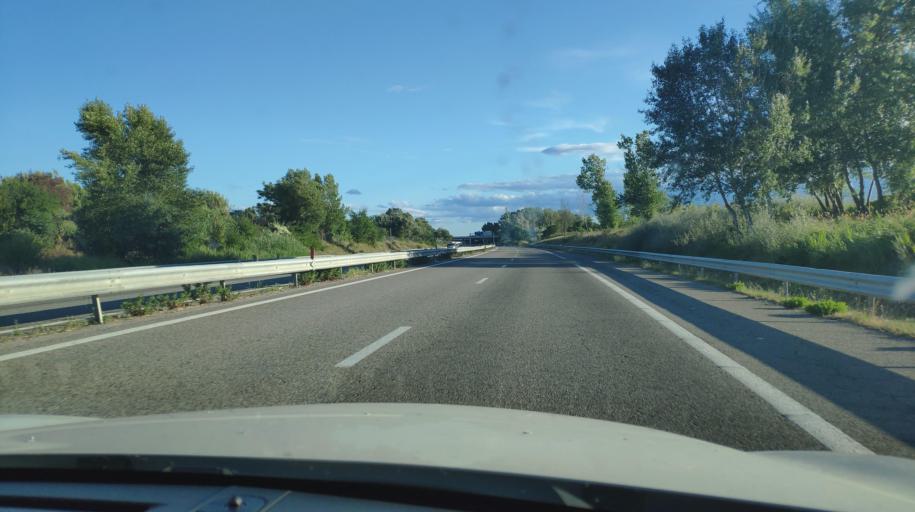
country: FR
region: Provence-Alpes-Cote d'Azur
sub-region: Departement des Alpes-de-Haute-Provence
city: Manosque
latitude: 43.8120
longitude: 5.8192
